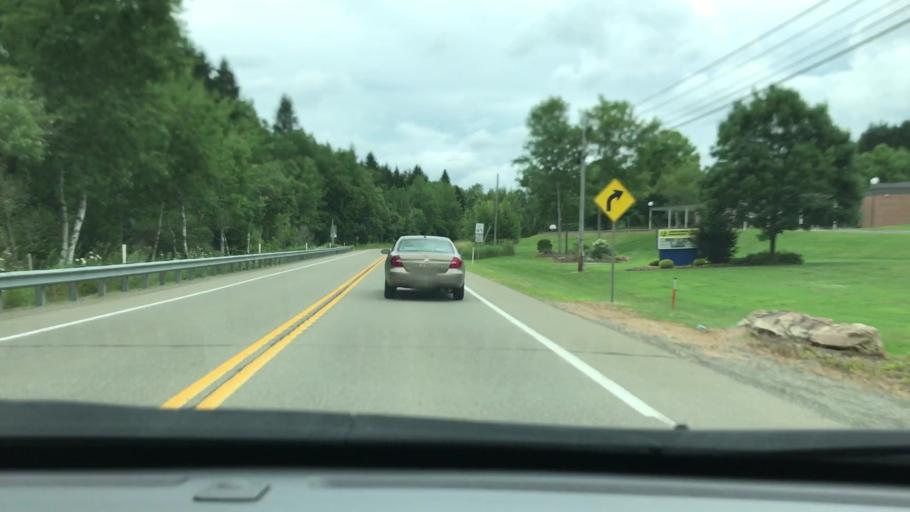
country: US
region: Pennsylvania
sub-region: Elk County
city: Johnsonburg
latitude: 41.5154
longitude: -78.6794
